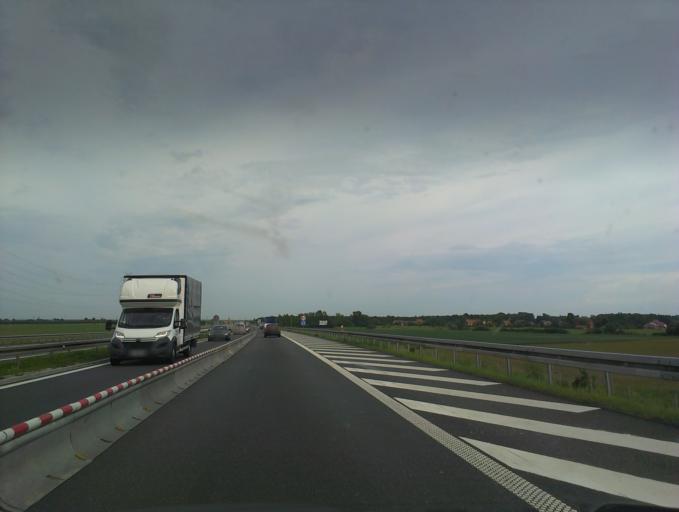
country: PL
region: Opole Voivodeship
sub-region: Powiat brzeski
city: Losiow
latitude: 50.7234
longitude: 17.5255
